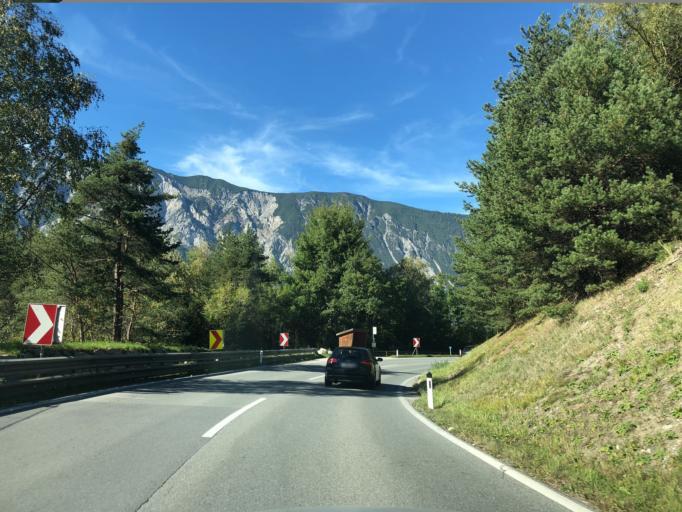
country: AT
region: Tyrol
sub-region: Politischer Bezirk Imst
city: Sautens
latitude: 47.2207
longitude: 10.8608
